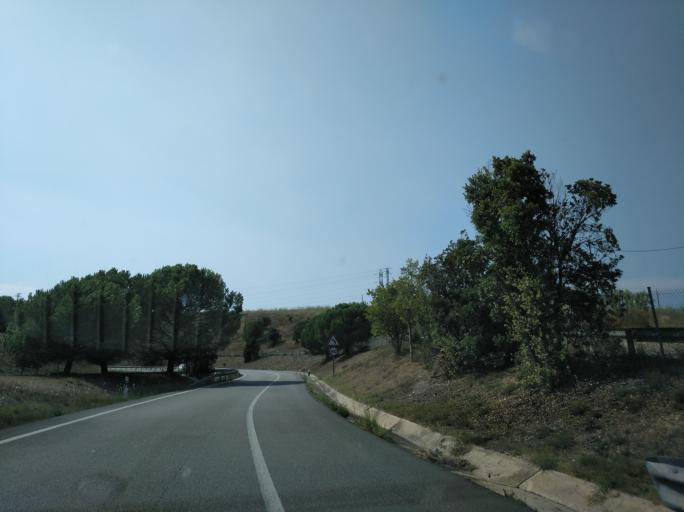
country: ES
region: Catalonia
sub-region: Provincia de Barcelona
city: La Roca del Valles
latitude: 41.6039
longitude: 2.3377
